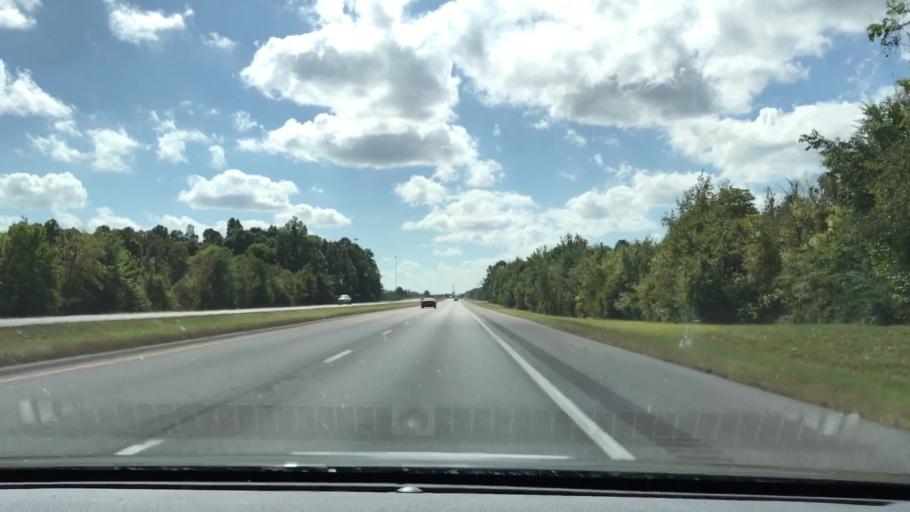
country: US
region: Kentucky
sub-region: McCracken County
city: Reidland
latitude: 37.0000
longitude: -88.5067
